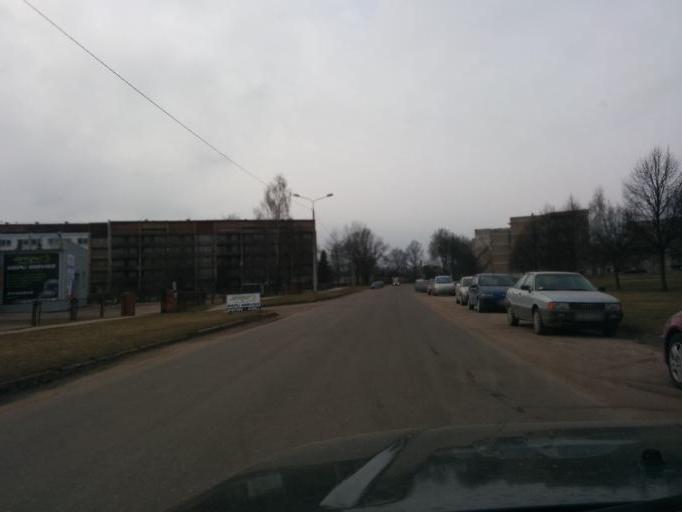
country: LV
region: Ozolnieku
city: Ozolnieki
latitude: 56.6657
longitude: 23.7645
